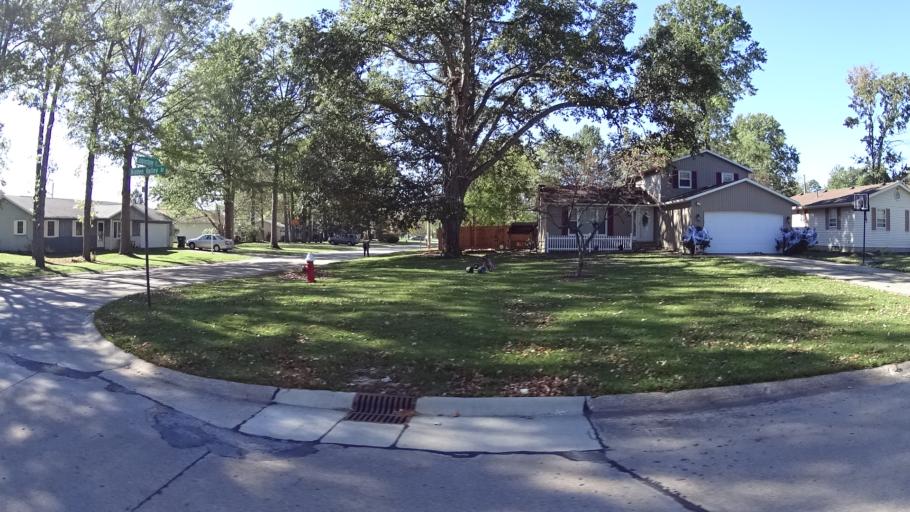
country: US
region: Ohio
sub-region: Lorain County
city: Amherst
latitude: 41.4012
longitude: -82.1900
